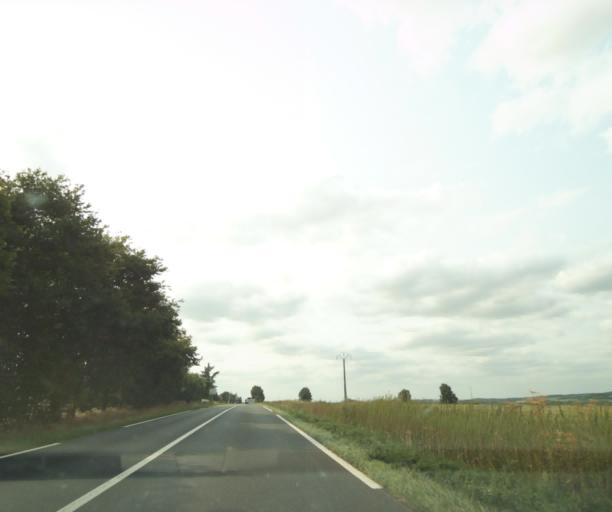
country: FR
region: Centre
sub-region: Departement de l'Indre
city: Clion
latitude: 46.9213
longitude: 1.3005
